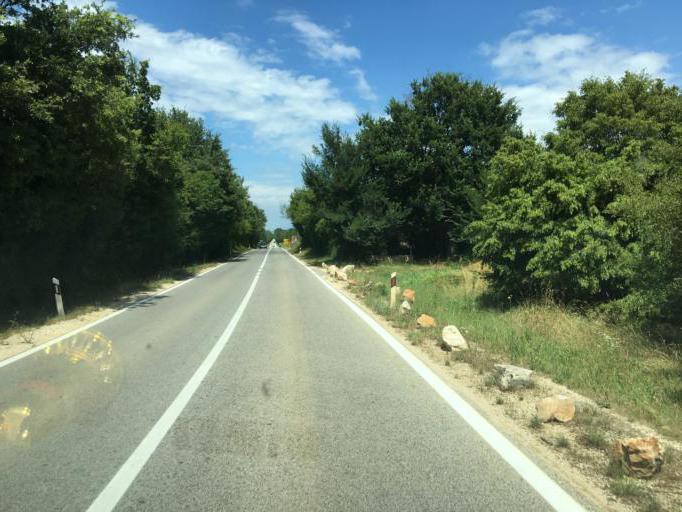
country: HR
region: Istarska
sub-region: Grad Rovinj
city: Rovinj
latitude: 45.1623
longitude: 13.7424
